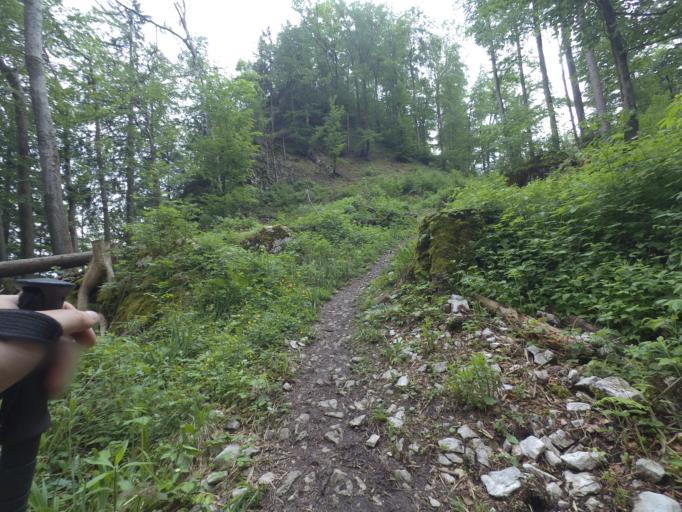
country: DE
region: Bavaria
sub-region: Upper Bavaria
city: Marktschellenberg
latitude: 47.7088
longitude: 13.0597
